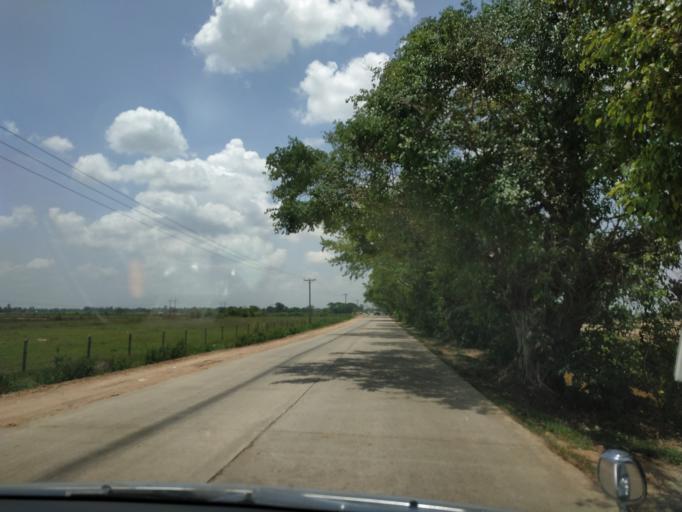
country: MM
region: Bago
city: Bago
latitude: 17.4790
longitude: 96.4928
